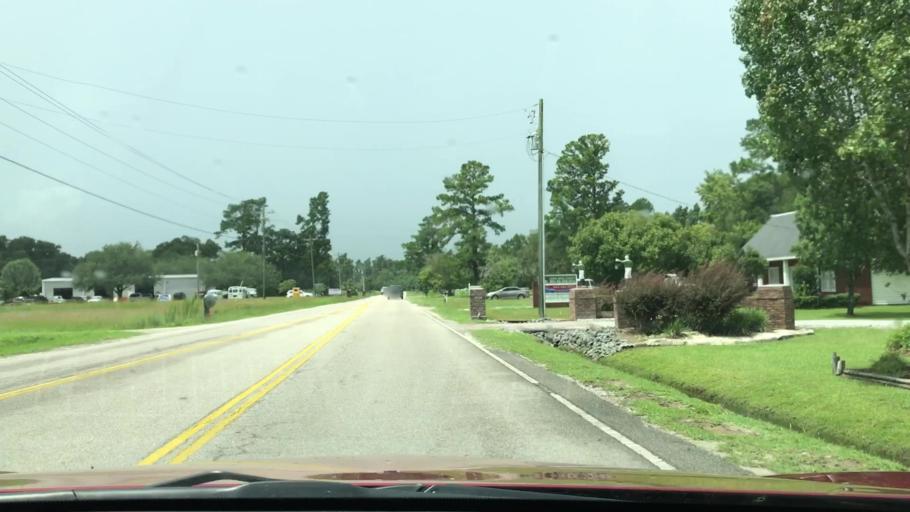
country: US
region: South Carolina
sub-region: Horry County
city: Red Hill
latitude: 33.8887
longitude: -78.9553
